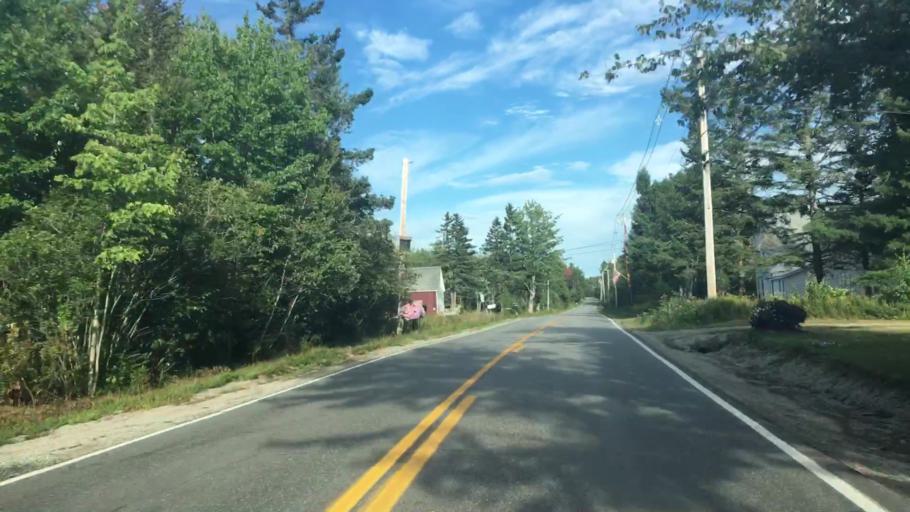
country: US
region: Maine
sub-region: Hancock County
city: Trenton
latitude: 44.4376
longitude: -68.3898
